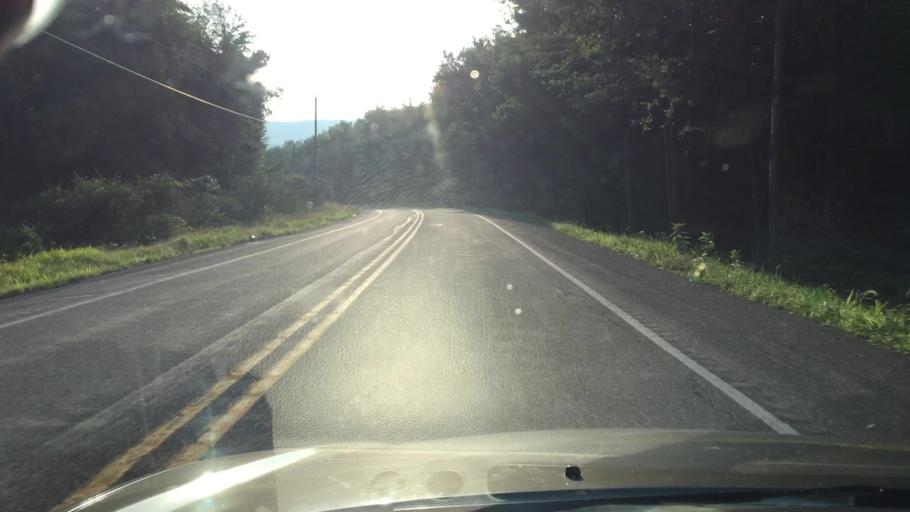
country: US
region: Pennsylvania
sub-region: Carbon County
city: Weatherly
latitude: 40.9117
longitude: -75.8364
